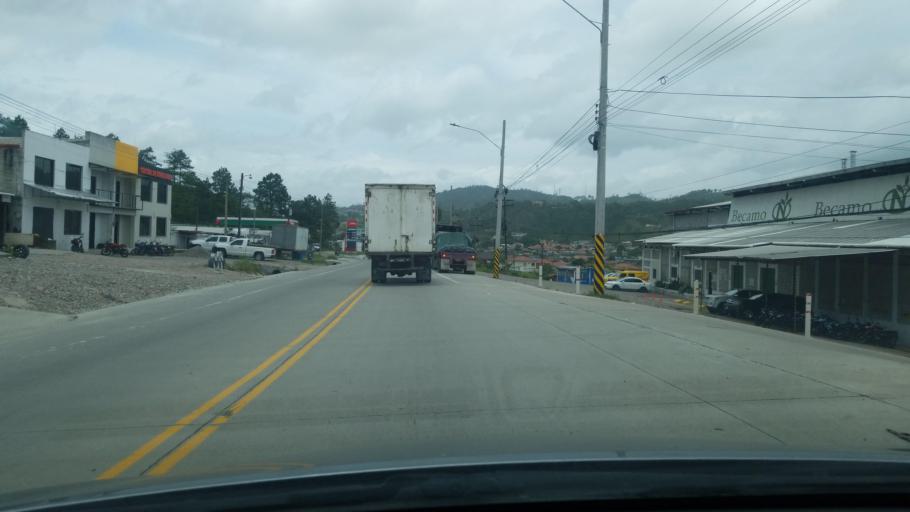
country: HN
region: Copan
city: Santa Rosa de Copan
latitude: 14.7867
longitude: -88.7803
